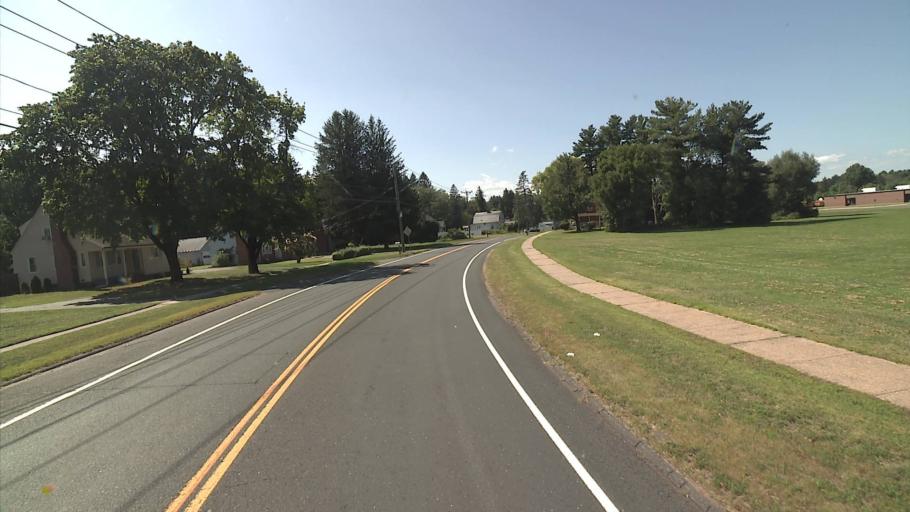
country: US
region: Connecticut
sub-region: Hartford County
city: Blue Hills
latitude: 41.8223
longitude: -72.7163
